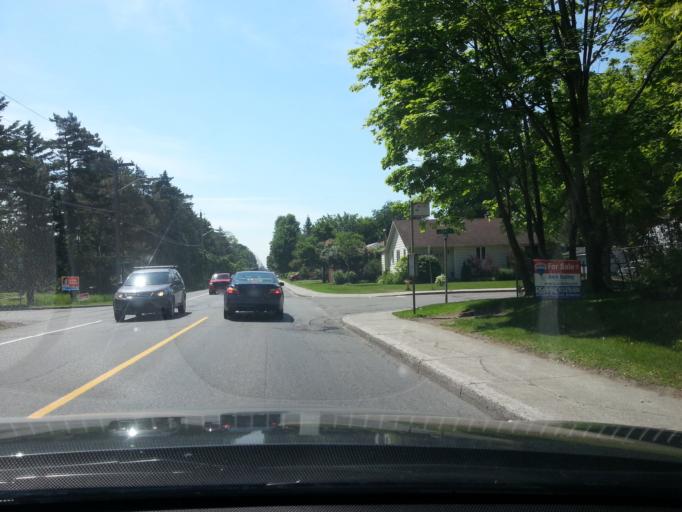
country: CA
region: Ontario
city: Ottawa
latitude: 45.3859
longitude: -75.7251
